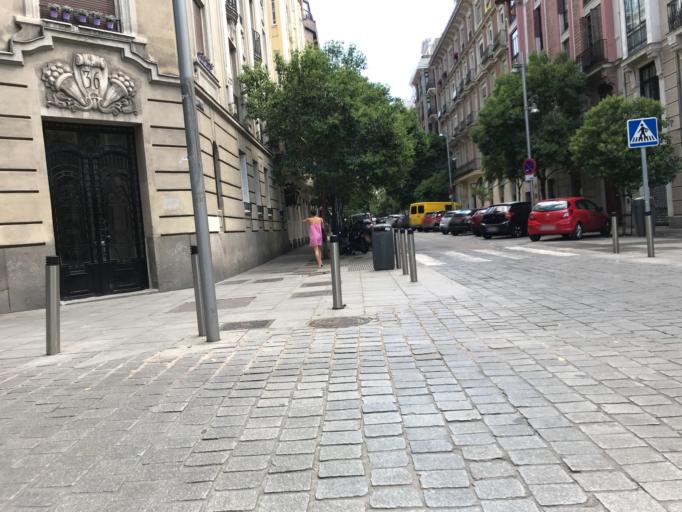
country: ES
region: Madrid
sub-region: Provincia de Madrid
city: Salamanca
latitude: 40.4238
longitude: -3.6830
